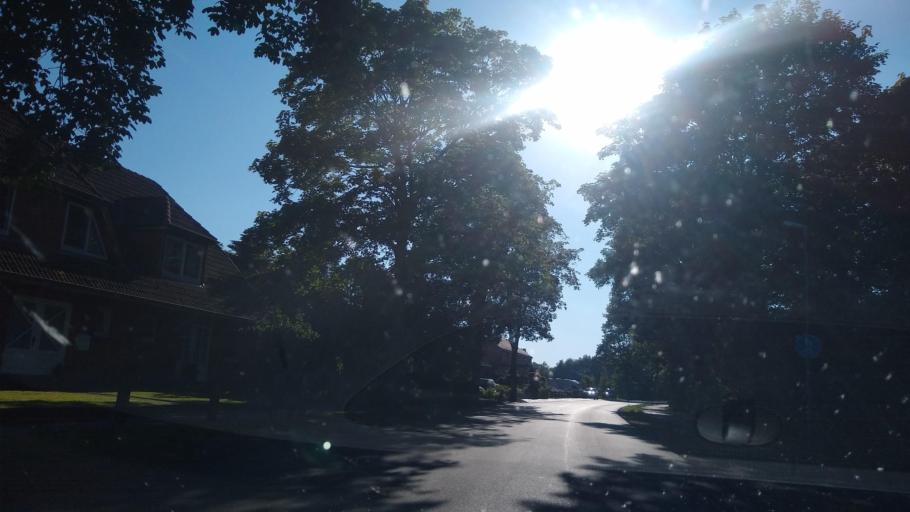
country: DE
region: Schleswig-Holstein
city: Gettorf
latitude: 54.4101
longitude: 9.9681
